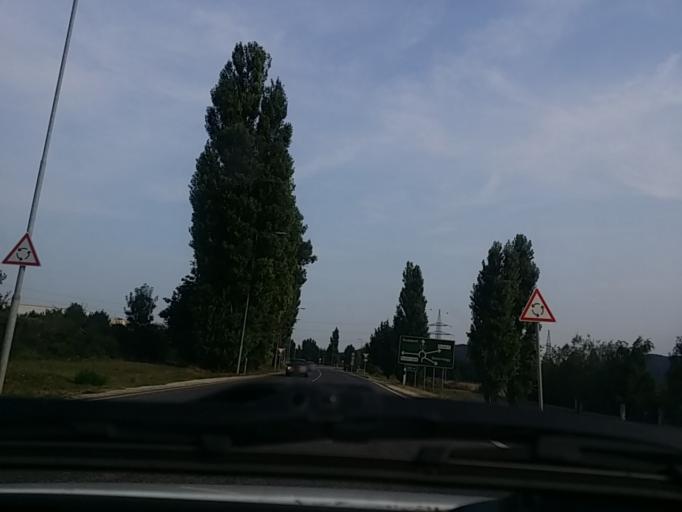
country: HU
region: Pest
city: Biatorbagy
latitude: 47.4768
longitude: 18.8413
